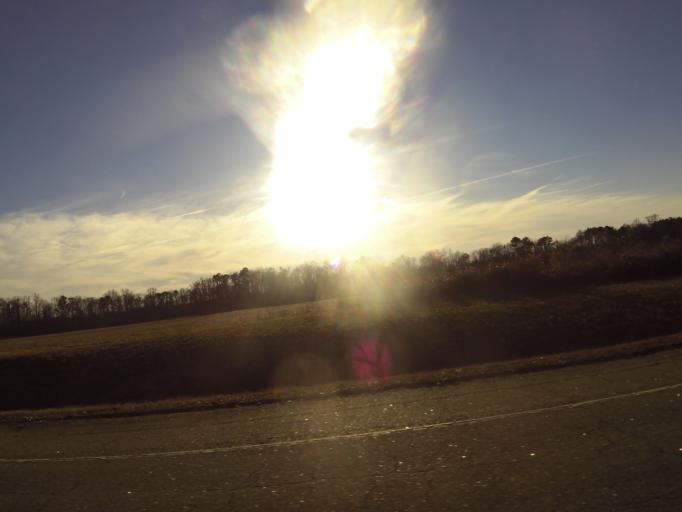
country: US
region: Virginia
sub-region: City of Franklin
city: Franklin
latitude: 36.6581
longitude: -76.8779
